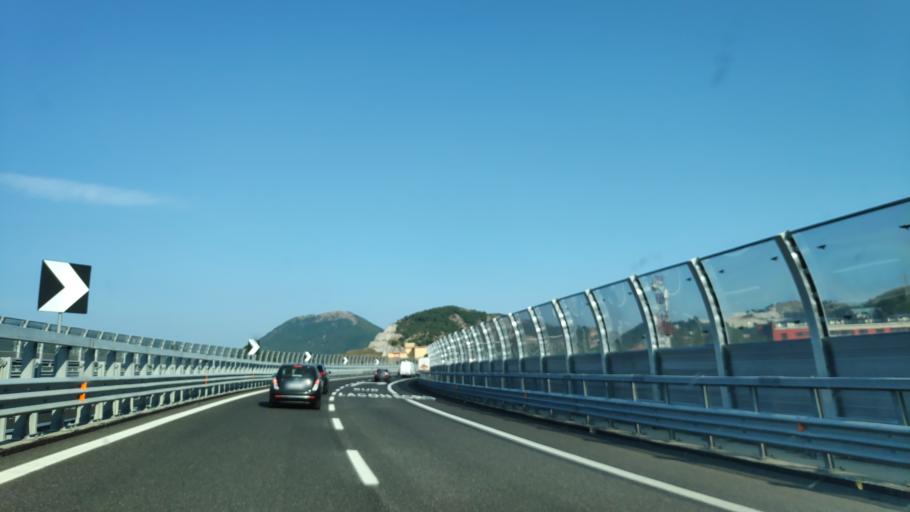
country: IT
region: Basilicate
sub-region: Provincia di Potenza
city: Lagonegro
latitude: 40.1307
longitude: 15.7639
